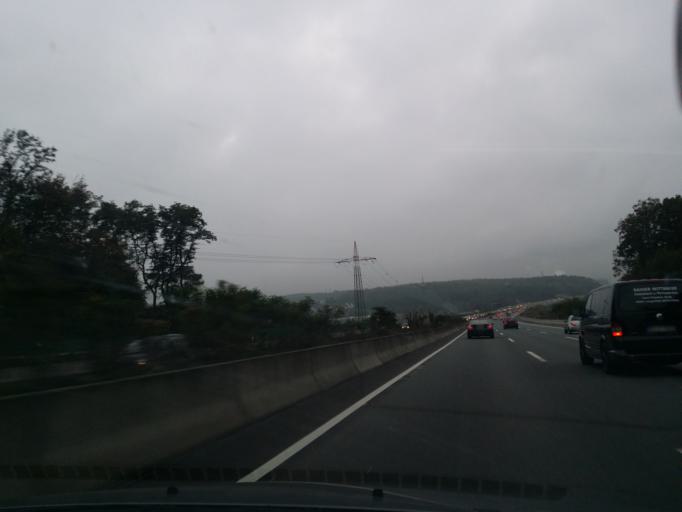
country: DE
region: North Rhine-Westphalia
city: Schwerte
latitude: 51.4193
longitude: 7.5132
